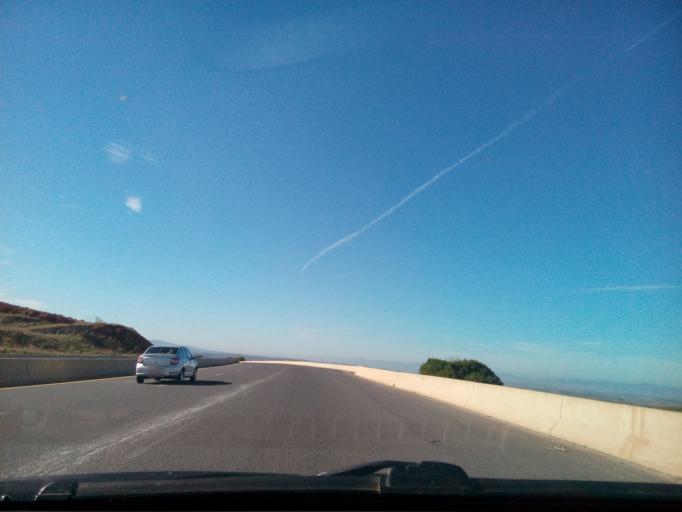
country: DZ
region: Tlemcen
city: Sidi Abdelli
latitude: 35.0197
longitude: -1.1442
